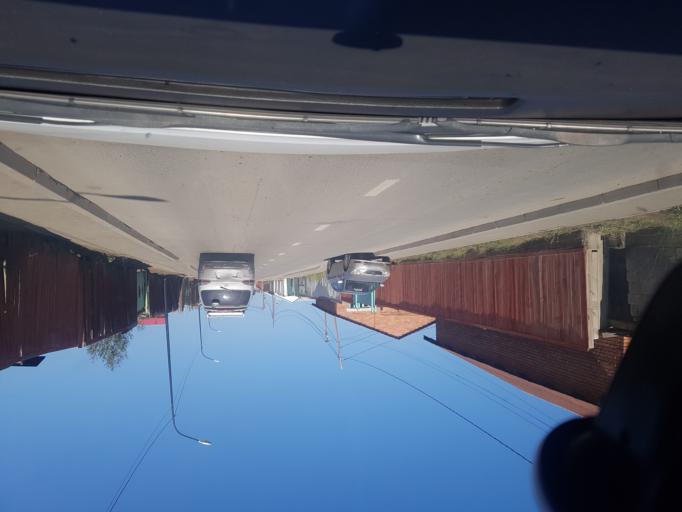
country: MN
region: Ulaanbaatar
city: Ulaanbaatar
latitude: 47.9501
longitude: 106.8632
